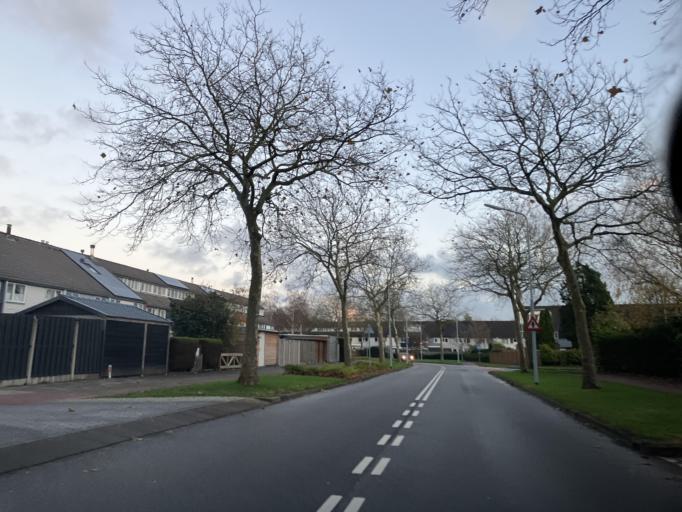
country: NL
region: South Holland
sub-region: Gemeente Hillegom
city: Hillegom
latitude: 52.2602
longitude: 4.6219
